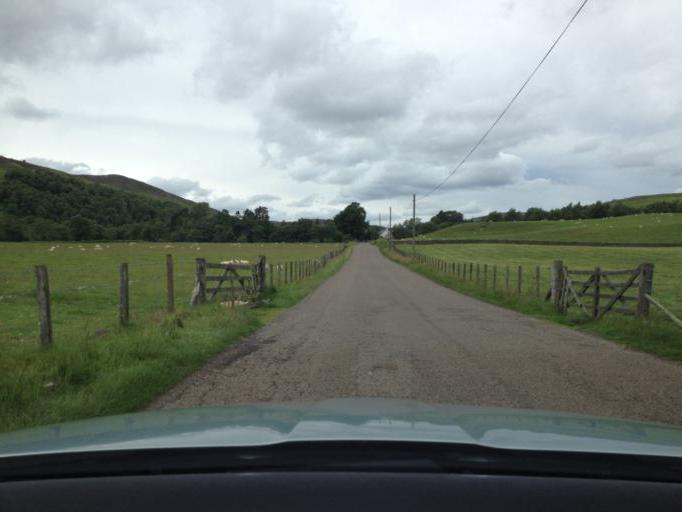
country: GB
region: Scotland
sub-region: Angus
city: Brechin
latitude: 56.8911
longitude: -2.7160
